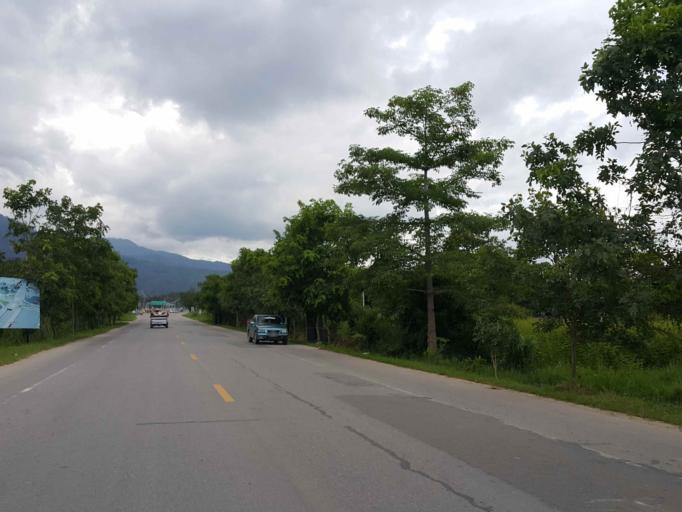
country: TH
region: Chiang Mai
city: San Sai
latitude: 18.8666
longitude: 98.9727
